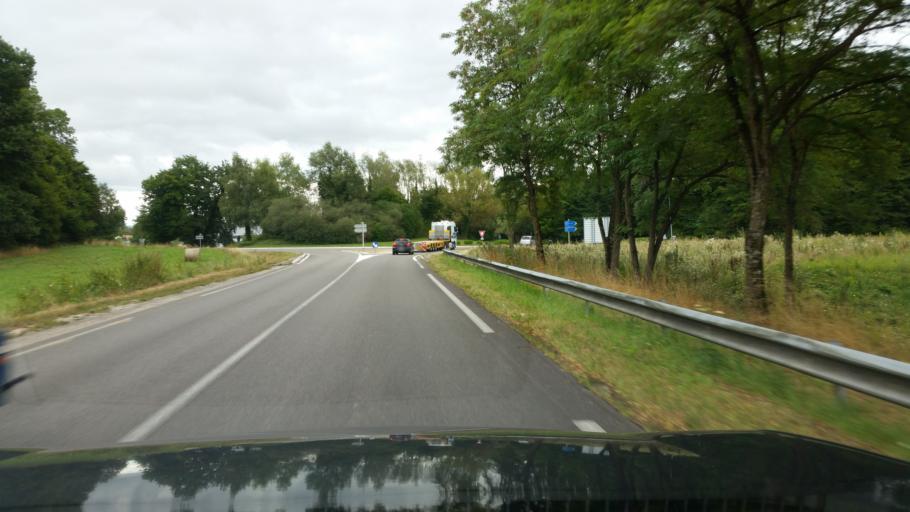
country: FR
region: Franche-Comte
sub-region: Departement du Jura
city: Bletterans
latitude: 46.6683
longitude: 5.4157
